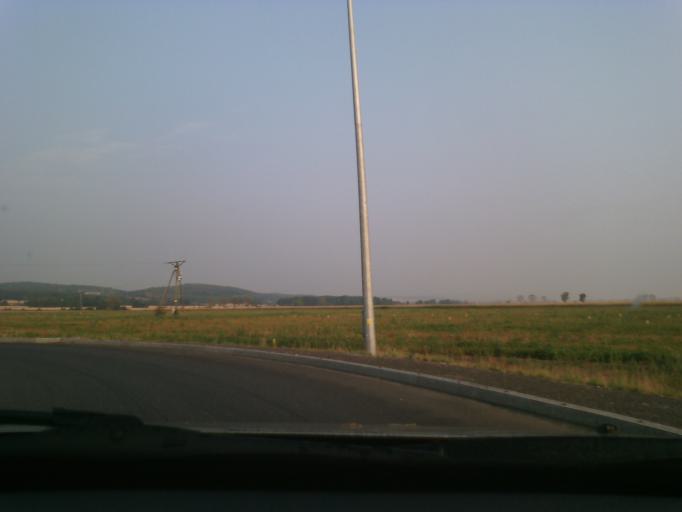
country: PL
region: Lower Silesian Voivodeship
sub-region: Powiat walbrzyski
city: Stare Bogaczowice
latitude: 50.9167
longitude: 16.2508
